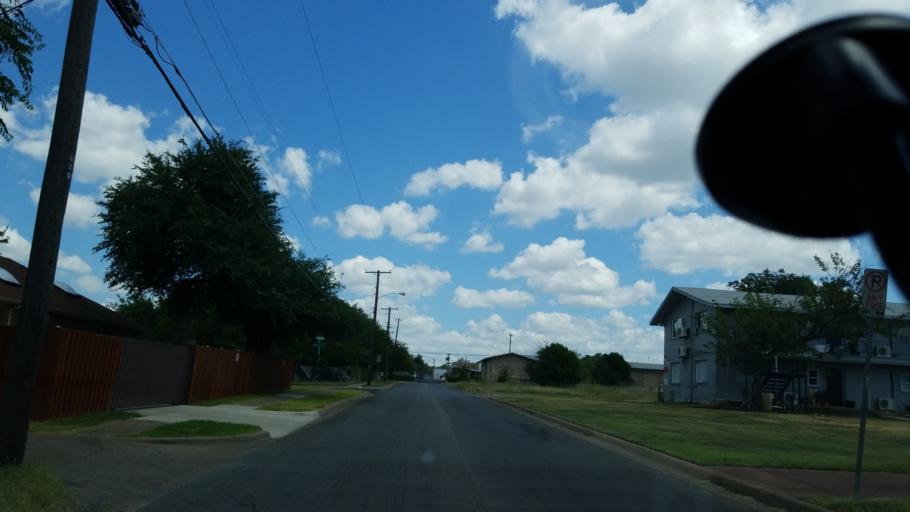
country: US
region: Texas
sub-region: Dallas County
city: Cockrell Hill
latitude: 32.7025
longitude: -96.8422
